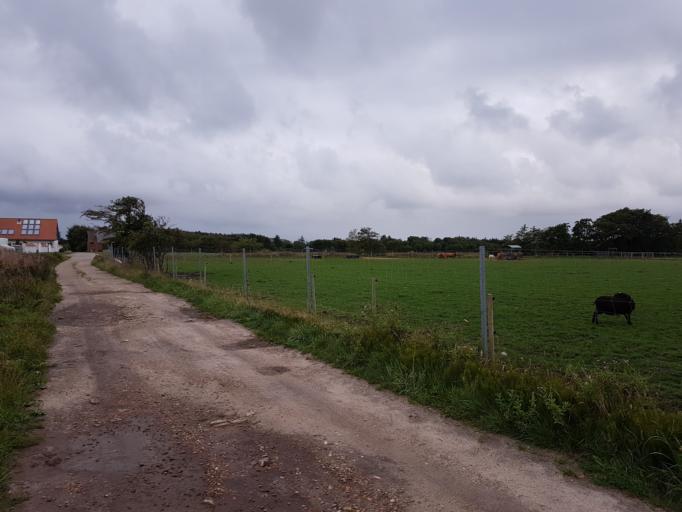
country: DK
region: Central Jutland
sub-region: Ringkobing-Skjern Kommune
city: Hvide Sande
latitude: 55.8531
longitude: 8.2925
